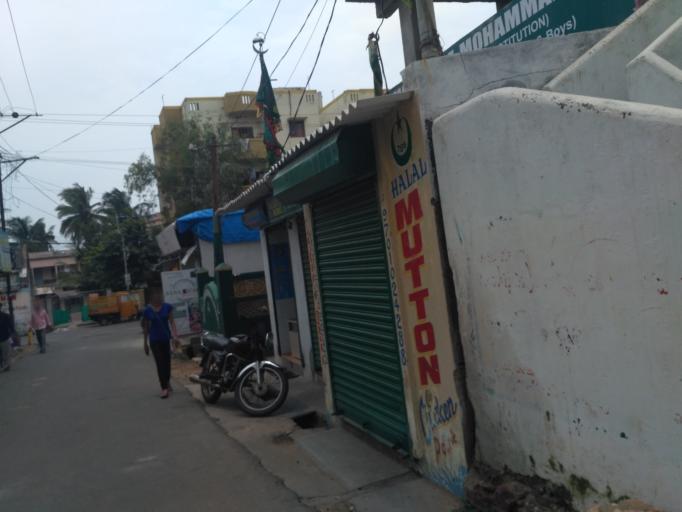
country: IN
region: Andhra Pradesh
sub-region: Vishakhapatnam
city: Yarada
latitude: 17.7239
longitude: 83.3324
